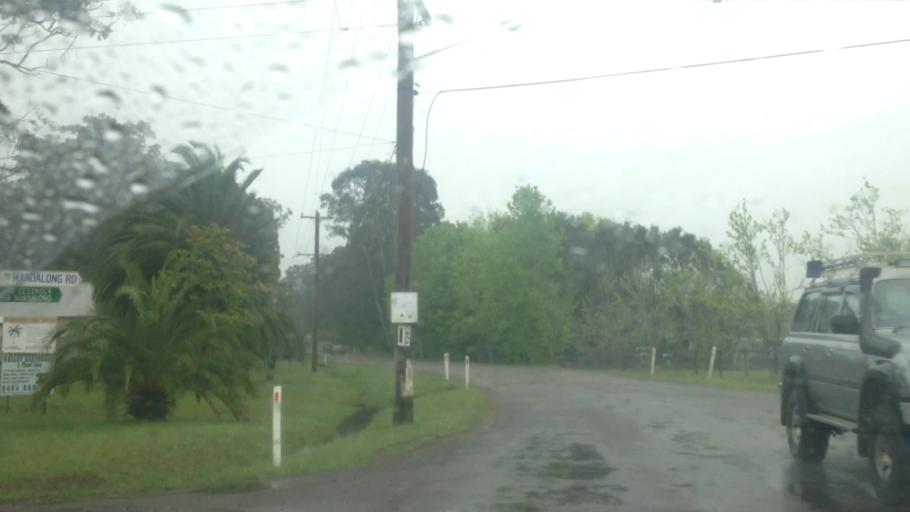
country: AU
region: New South Wales
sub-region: Wyong Shire
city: Little Jilliby
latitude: -33.1897
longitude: 151.3552
